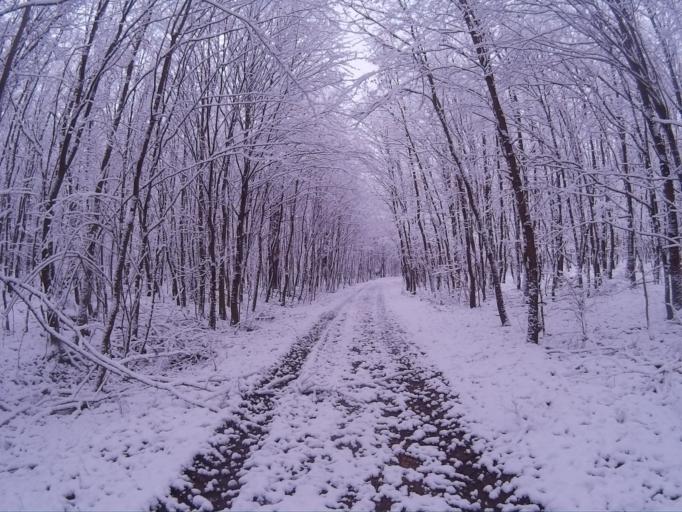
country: HU
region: Komarom-Esztergom
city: Tarjan
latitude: 47.5800
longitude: 18.4860
